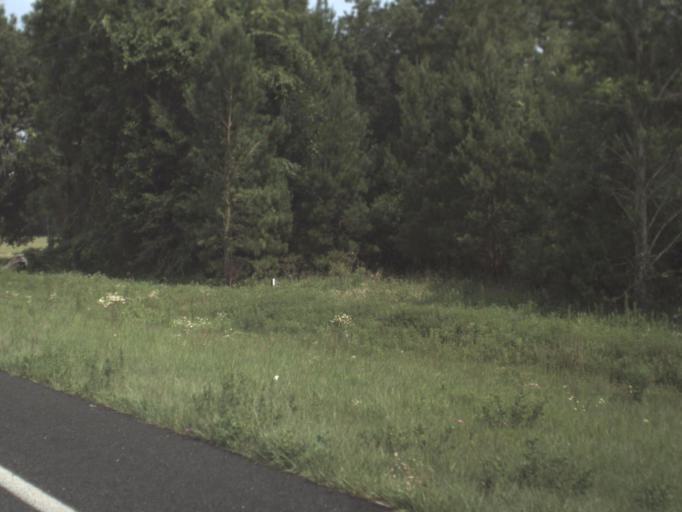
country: US
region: Florida
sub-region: Levy County
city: Williston
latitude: 29.3960
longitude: -82.4894
